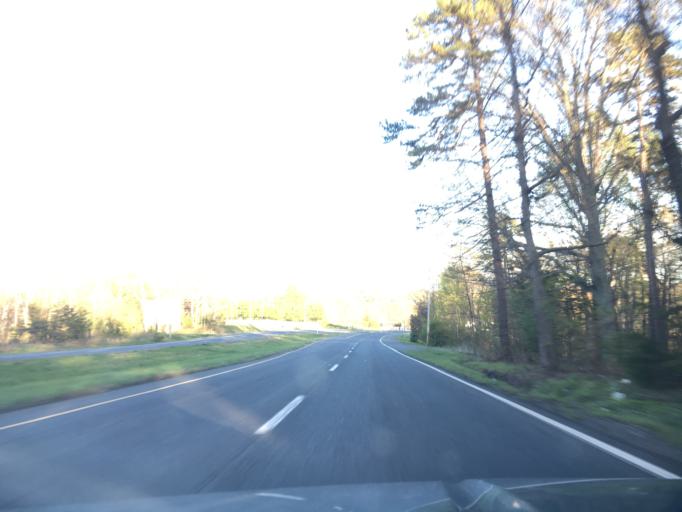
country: US
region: Virginia
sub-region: City of Lynchburg
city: Lynchburg
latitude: 37.3750
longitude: -79.1231
